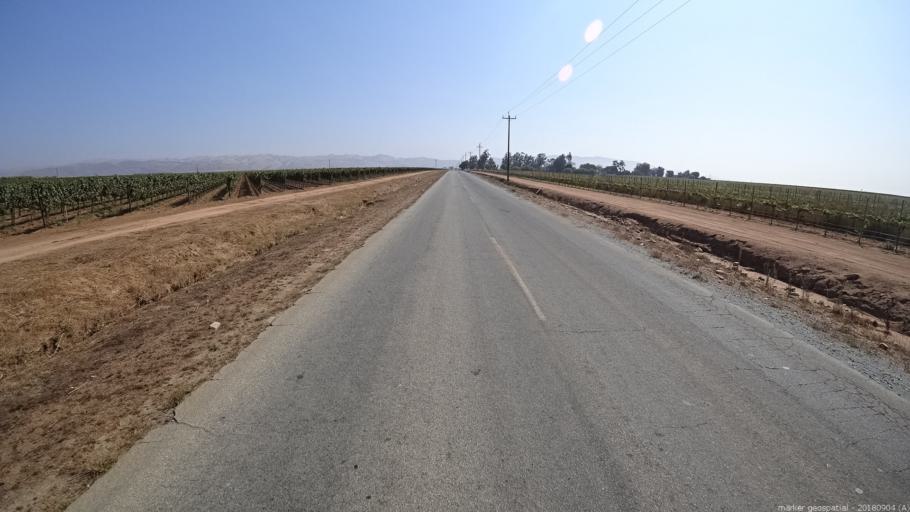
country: US
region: California
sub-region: Monterey County
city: Gonzales
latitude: 36.4989
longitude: -121.4069
